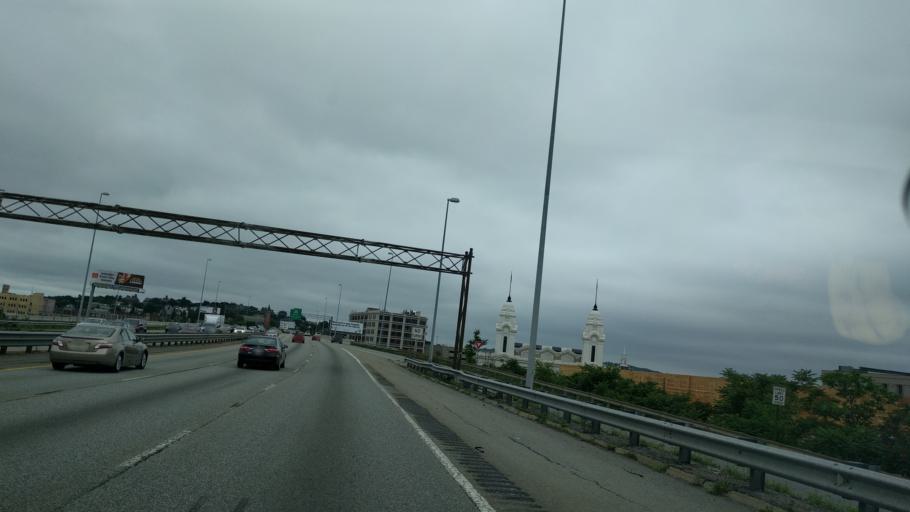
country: US
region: Massachusetts
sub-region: Worcester County
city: Worcester
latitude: 42.2640
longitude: -71.7937
